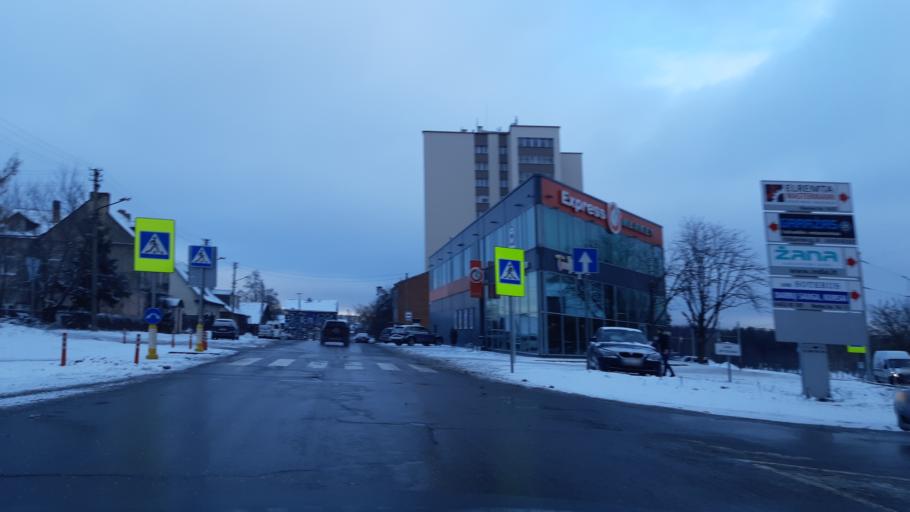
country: LT
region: Kauno apskritis
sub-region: Kaunas
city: Kaunas
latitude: 54.9049
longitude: 23.8884
